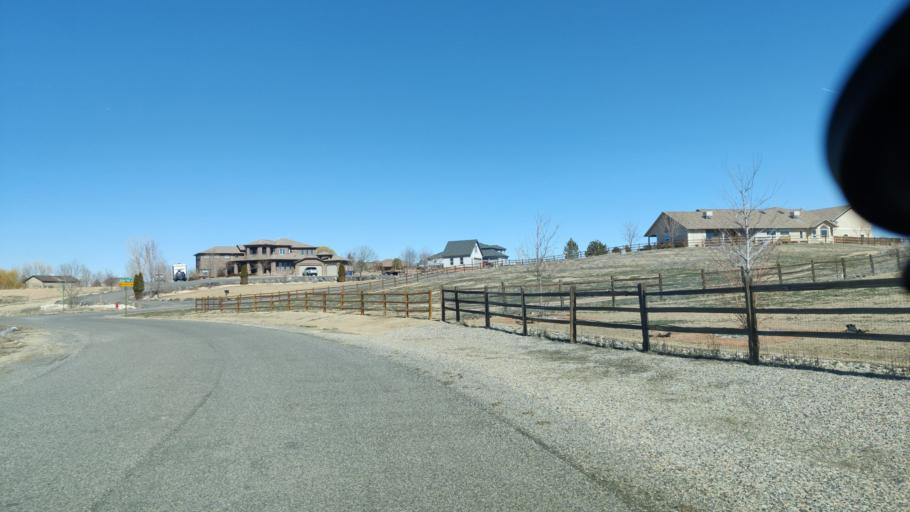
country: US
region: Colorado
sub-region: Mesa County
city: Fruita
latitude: 39.2067
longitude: -108.7080
